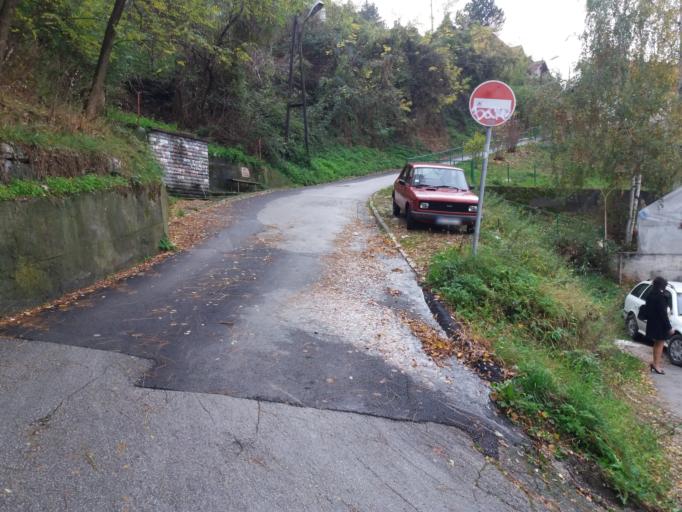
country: RS
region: Central Serbia
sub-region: Zlatiborski Okrug
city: Uzice
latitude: 43.8520
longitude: 19.8397
